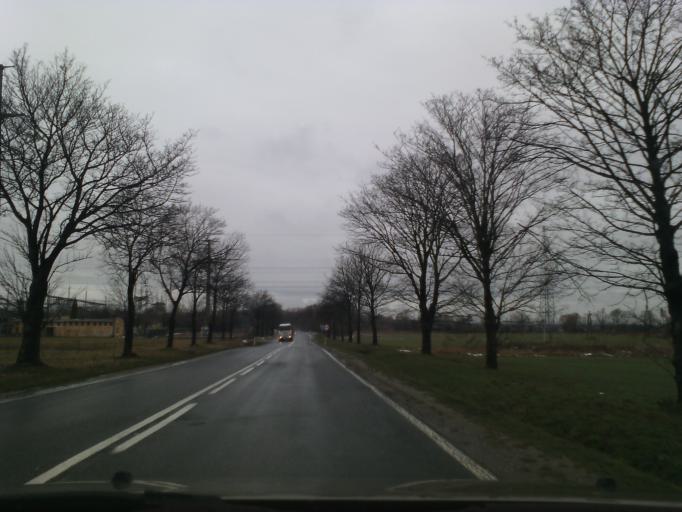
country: PL
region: Lower Silesian Voivodeship
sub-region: Powiat swidnicki
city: Swiebodzice
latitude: 50.8546
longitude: 16.3559
